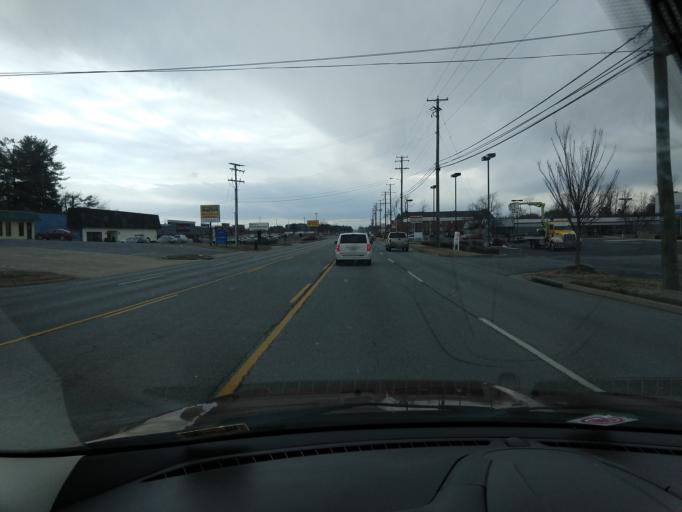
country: US
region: Virginia
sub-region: City of Waynesboro
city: Waynesboro
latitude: 38.0791
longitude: -78.9212
